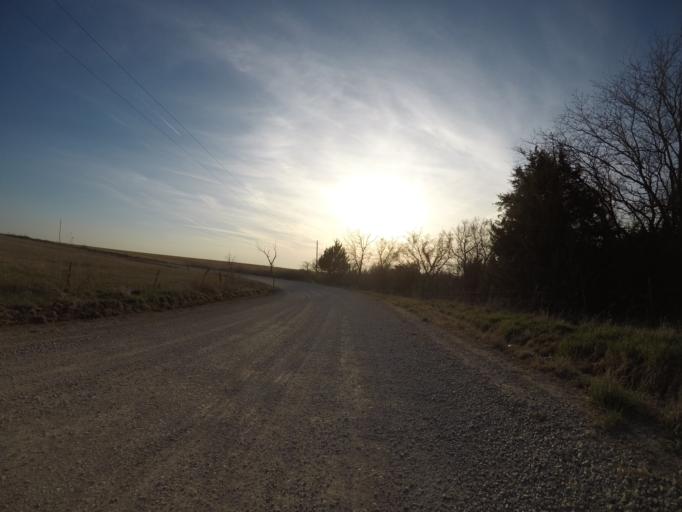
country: US
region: Kansas
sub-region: Riley County
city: Ogden
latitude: 39.2435
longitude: -96.6949
